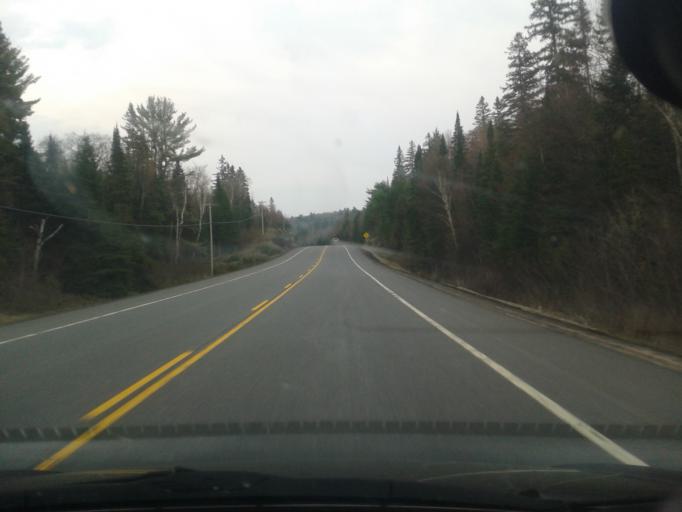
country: CA
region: Ontario
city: Huntsville
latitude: 45.4707
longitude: -78.7783
